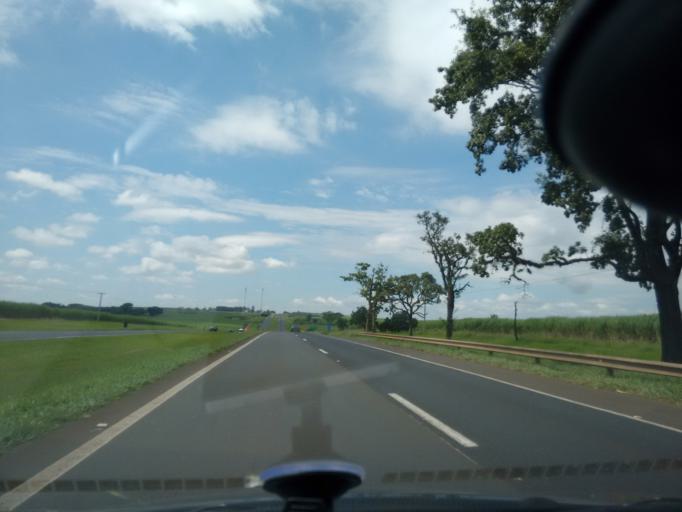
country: BR
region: Sao Paulo
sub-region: Ibate
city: Ibate
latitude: -21.9072
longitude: -48.0531
